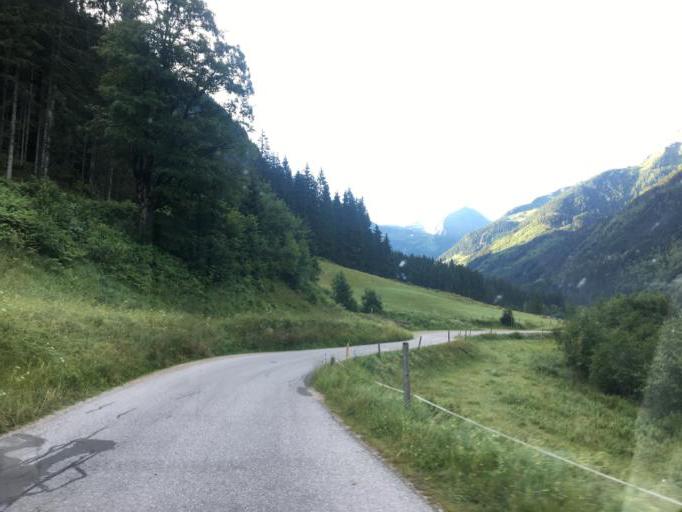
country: AT
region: Styria
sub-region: Politischer Bezirk Liezen
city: Schladming
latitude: 47.3541
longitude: 13.7215
